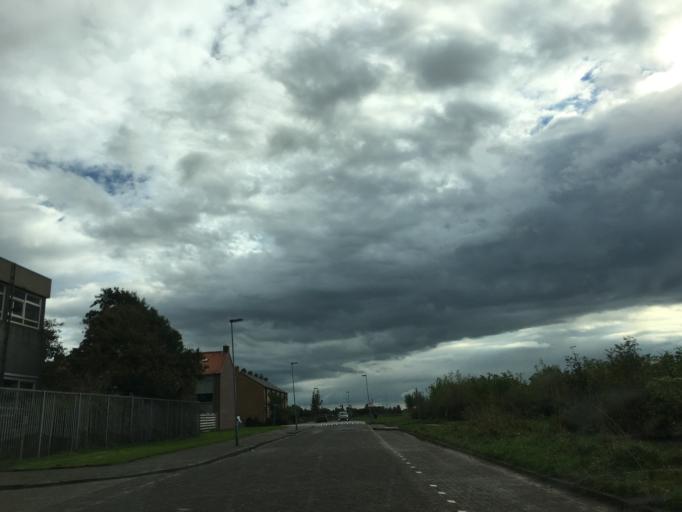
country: NL
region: North Holland
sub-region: Gemeente Den Helder
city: Den Helder
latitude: 52.9309
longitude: 4.7664
